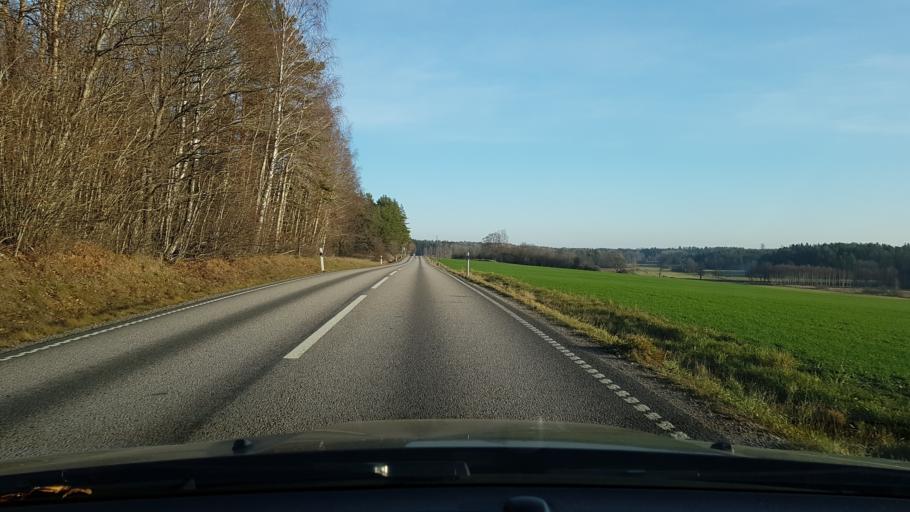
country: SE
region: Stockholm
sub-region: Norrtalje Kommun
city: Nykvarn
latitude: 59.7395
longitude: 18.1808
